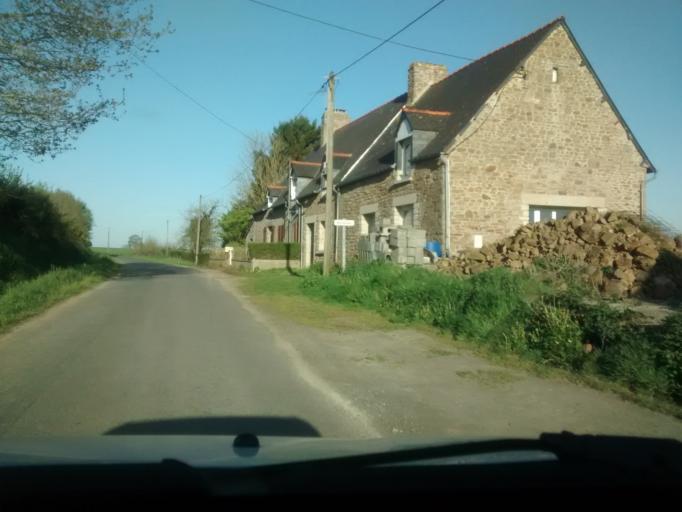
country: FR
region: Brittany
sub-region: Departement d'Ille-et-Vilaine
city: Roz-sur-Couesnon
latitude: 48.5527
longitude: -1.6155
